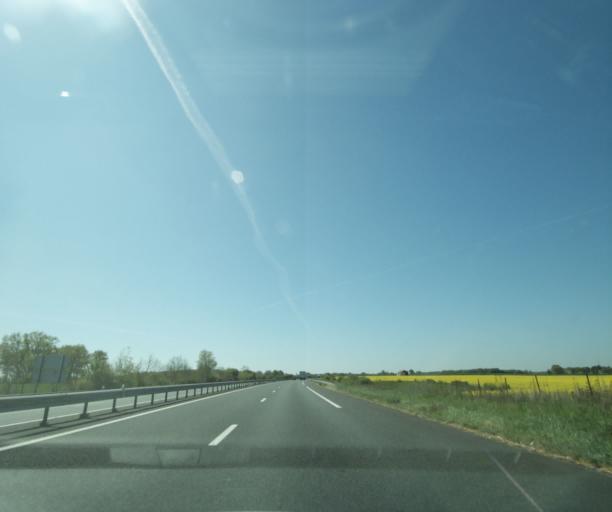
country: FR
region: Centre
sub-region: Departement de l'Indre
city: Luant
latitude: 46.6587
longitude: 1.5695
